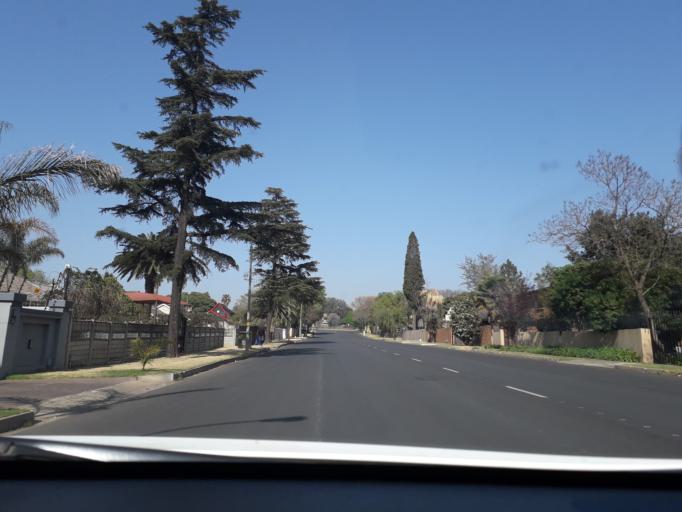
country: ZA
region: Gauteng
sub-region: City of Johannesburg Metropolitan Municipality
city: Modderfontein
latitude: -26.0895
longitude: 28.2465
